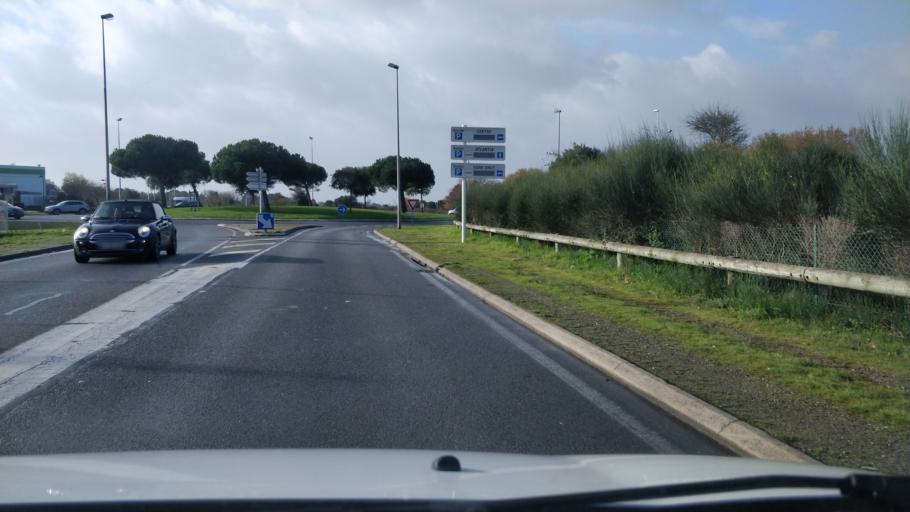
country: FR
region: Pays de la Loire
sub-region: Departement de la Loire-Atlantique
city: La Baule-Escoublac
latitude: 47.2948
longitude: -2.3973
